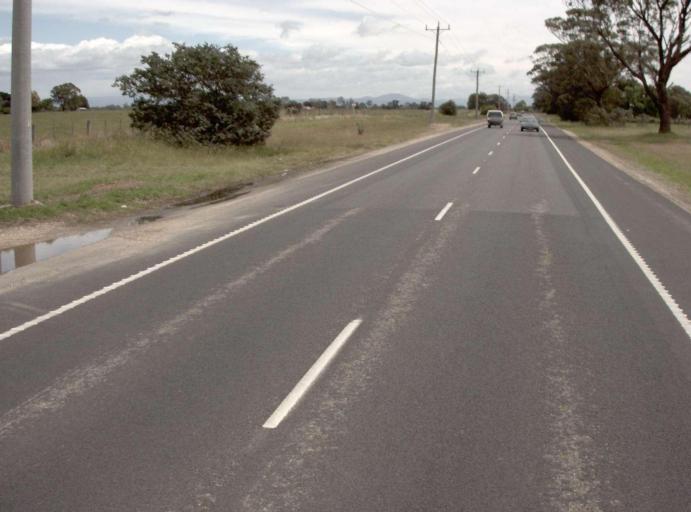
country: AU
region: Victoria
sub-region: Wellington
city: Sale
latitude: -38.0609
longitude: 147.0283
